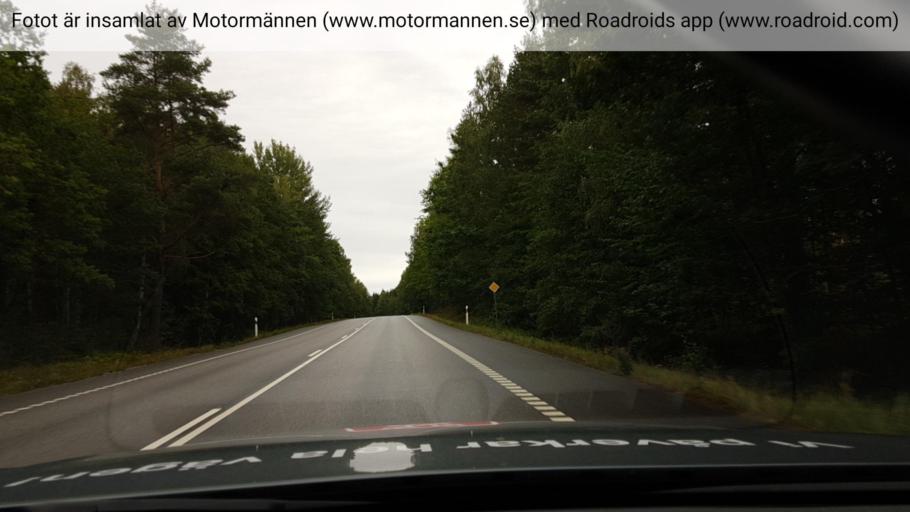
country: SE
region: Soedermanland
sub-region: Trosa Kommun
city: Vagnharad
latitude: 58.9708
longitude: 17.5724
